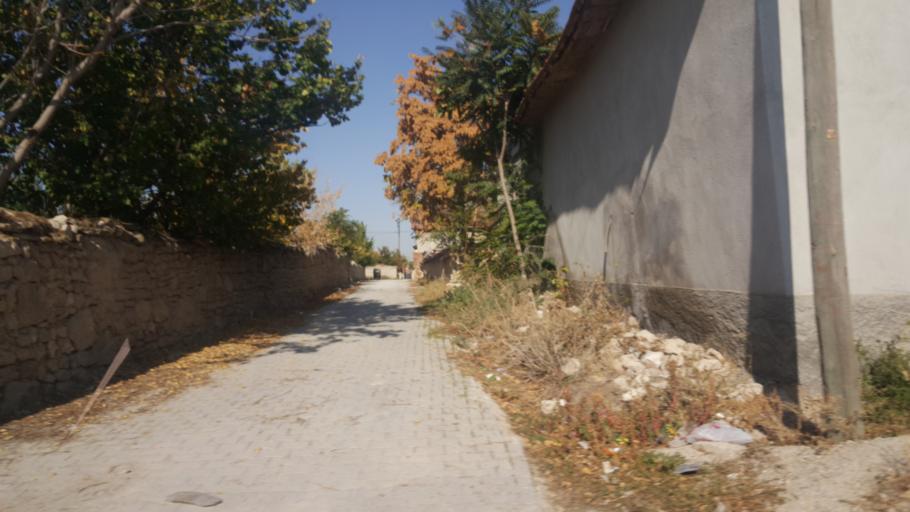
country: TR
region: Konya
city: Celtik
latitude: 39.0588
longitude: 31.8384
